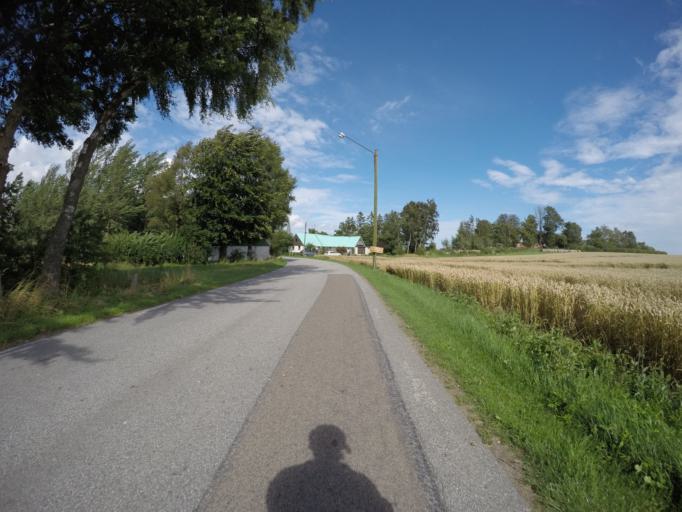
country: SE
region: Skane
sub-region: Simrishamns Kommun
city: Simrishamn
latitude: 55.4958
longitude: 14.2026
